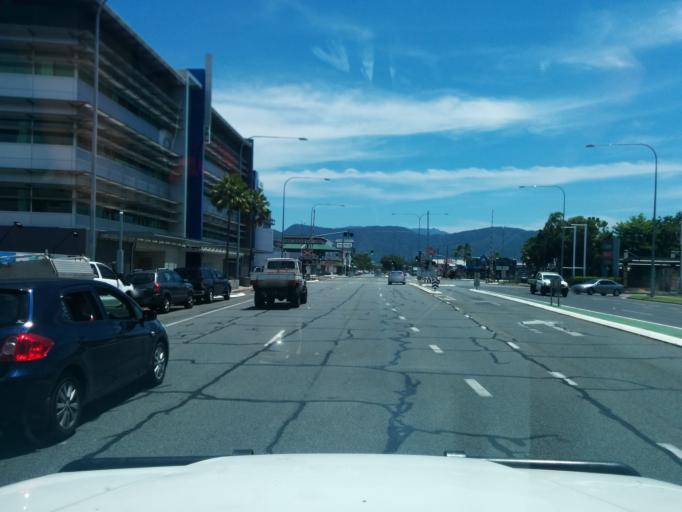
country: AU
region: Queensland
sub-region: Cairns
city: Cairns
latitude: -16.9269
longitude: 145.7734
